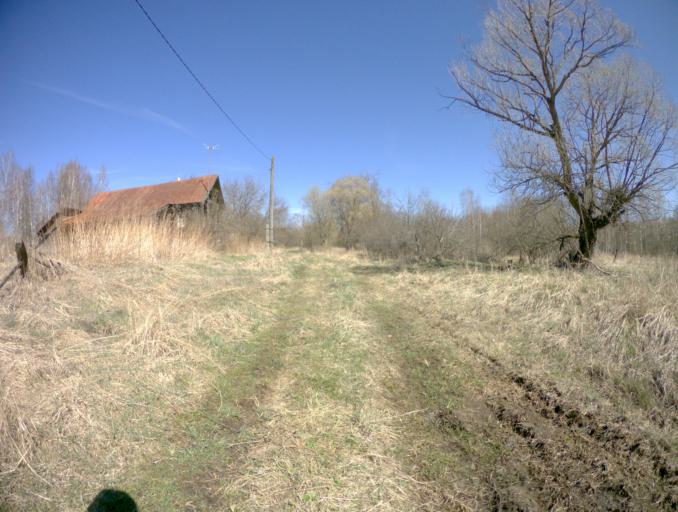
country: RU
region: Vladimir
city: Ivanishchi
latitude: 55.8642
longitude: 40.4350
